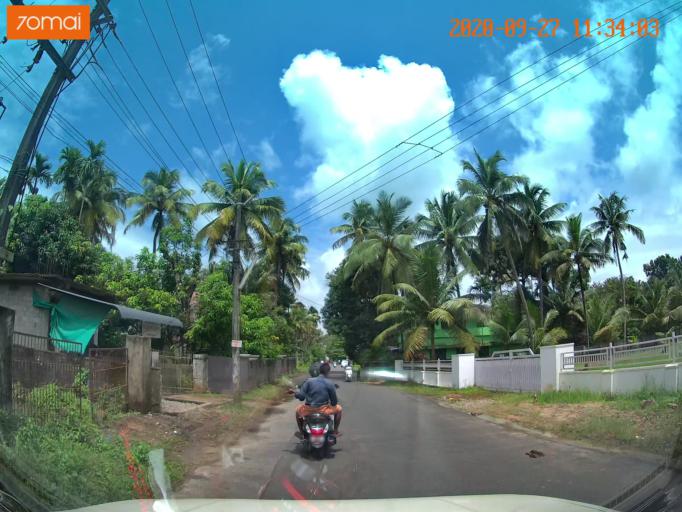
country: IN
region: Kerala
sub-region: Thrissur District
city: Thanniyam
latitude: 10.4350
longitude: 76.1274
